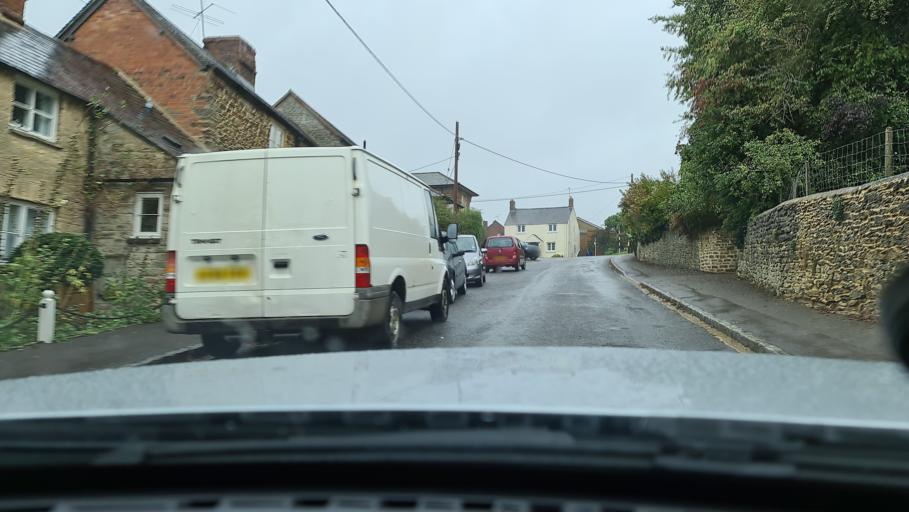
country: GB
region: England
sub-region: Oxfordshire
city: Somerton
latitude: 51.9279
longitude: -1.3089
